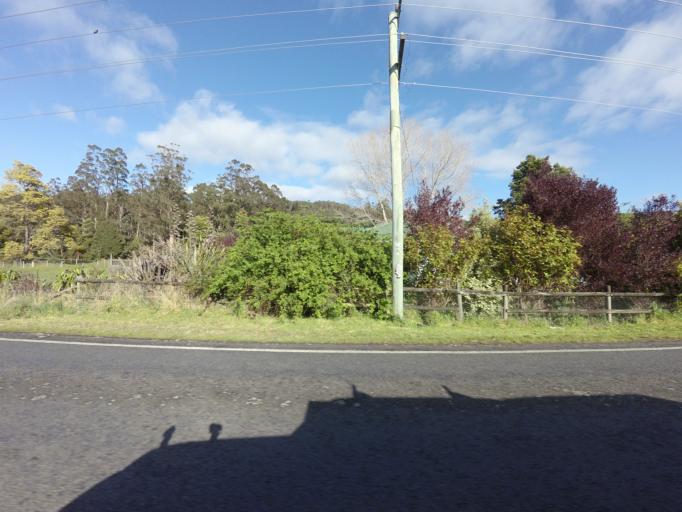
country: AU
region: Tasmania
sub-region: Huon Valley
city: Cygnet
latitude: -43.2895
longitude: 147.0107
